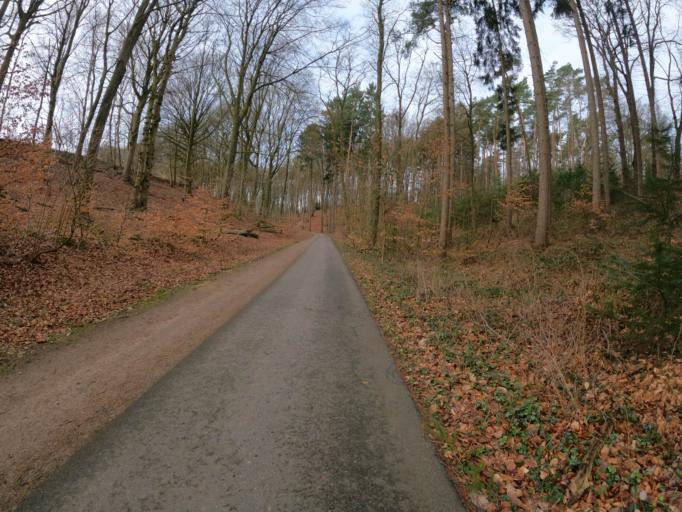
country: DE
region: Lower Saxony
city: Seevetal
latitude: 53.4458
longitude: 9.9089
